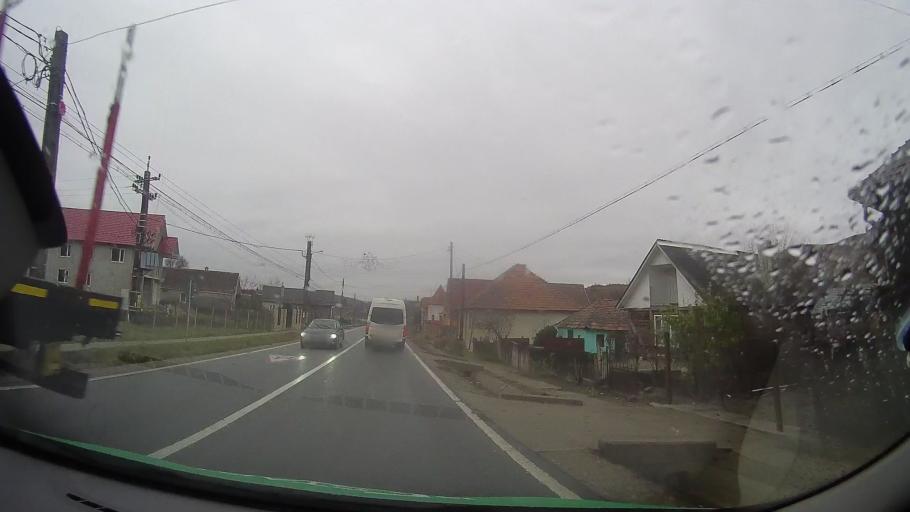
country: RO
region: Bistrita-Nasaud
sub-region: Comuna Galatii Bistritei
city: Galatii Bistritei
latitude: 47.0180
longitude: 24.4123
